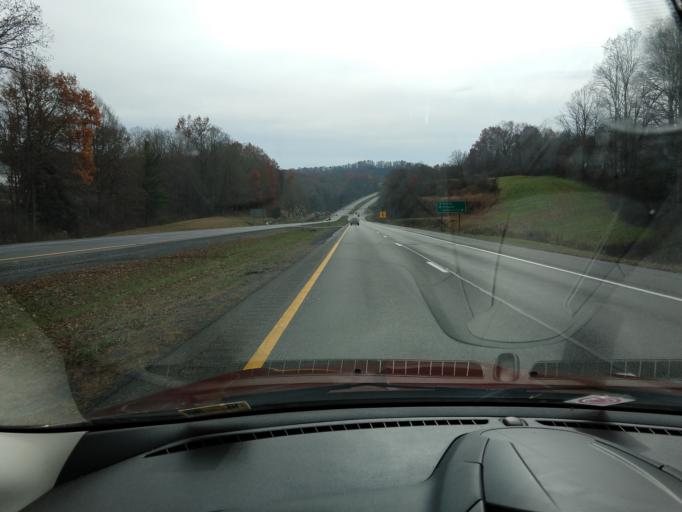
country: US
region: West Virginia
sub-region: Nicholas County
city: Summersville
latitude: 38.2811
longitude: -80.8345
